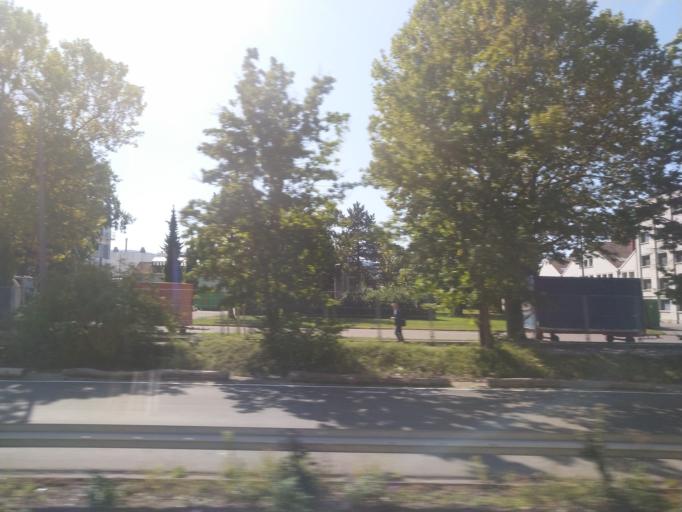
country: CH
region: Basel-City
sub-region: Basel-Stadt
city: Bettingen
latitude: 47.5507
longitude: 7.6614
